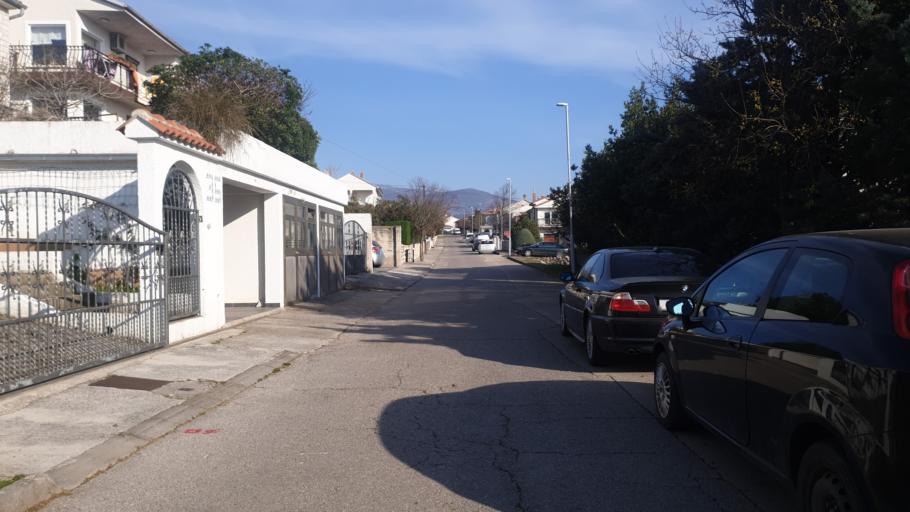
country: HR
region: Primorsko-Goranska
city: Novi Vinodolski
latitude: 45.1244
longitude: 14.8039
